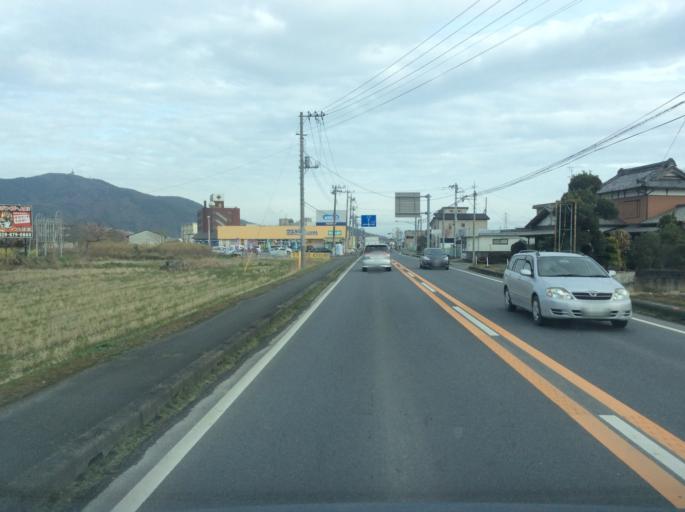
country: JP
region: Ibaraki
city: Tsukuba
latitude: 36.1782
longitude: 140.0833
